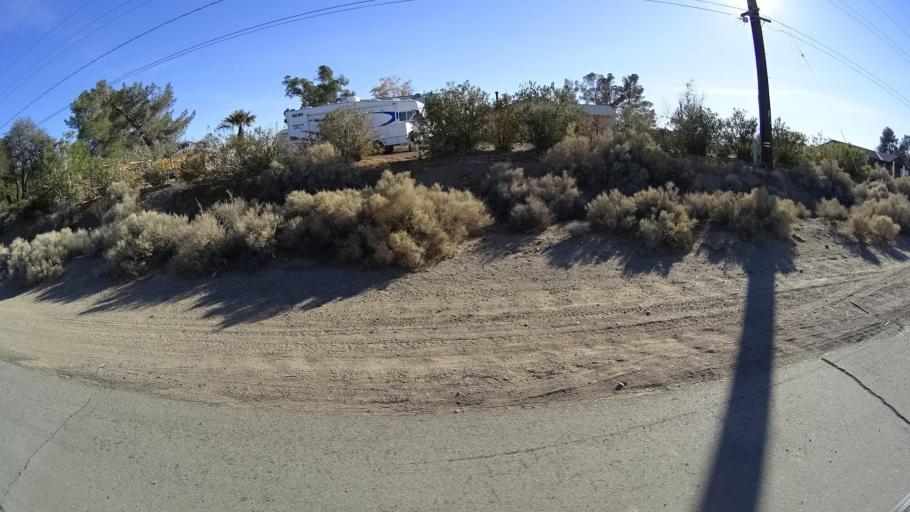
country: US
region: California
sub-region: Kern County
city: Ridgecrest
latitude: 35.6225
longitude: -117.7142
